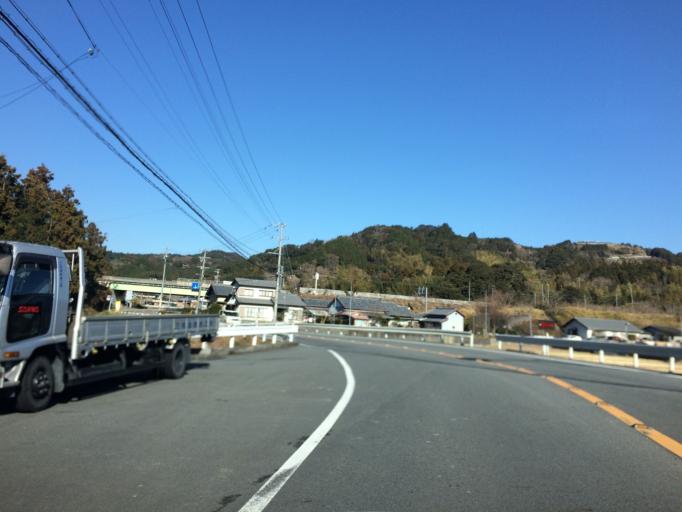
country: JP
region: Shizuoka
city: Shimada
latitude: 34.8525
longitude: 138.2037
